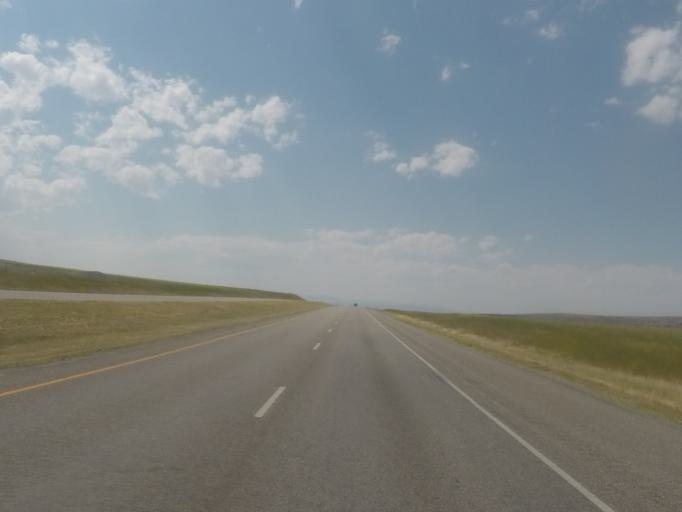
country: US
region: Montana
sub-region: Gallatin County
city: Manhattan
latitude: 45.8723
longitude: -111.3877
